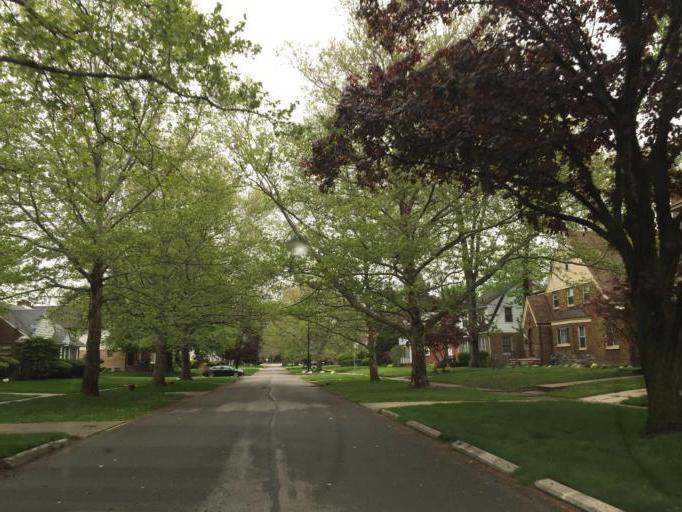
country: US
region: Michigan
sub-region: Oakland County
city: Southfield
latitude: 42.4128
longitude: -83.2330
